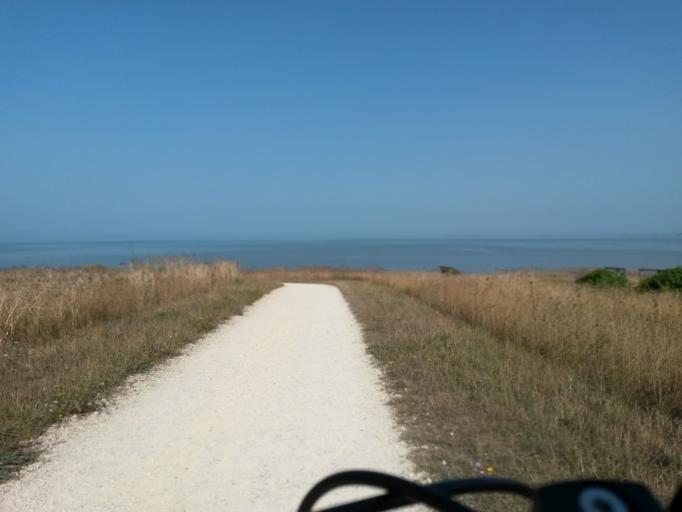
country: FR
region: Poitou-Charentes
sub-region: Departement de la Charente-Maritime
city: Nieul-sur-Mer
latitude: 46.2139
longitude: -1.1942
